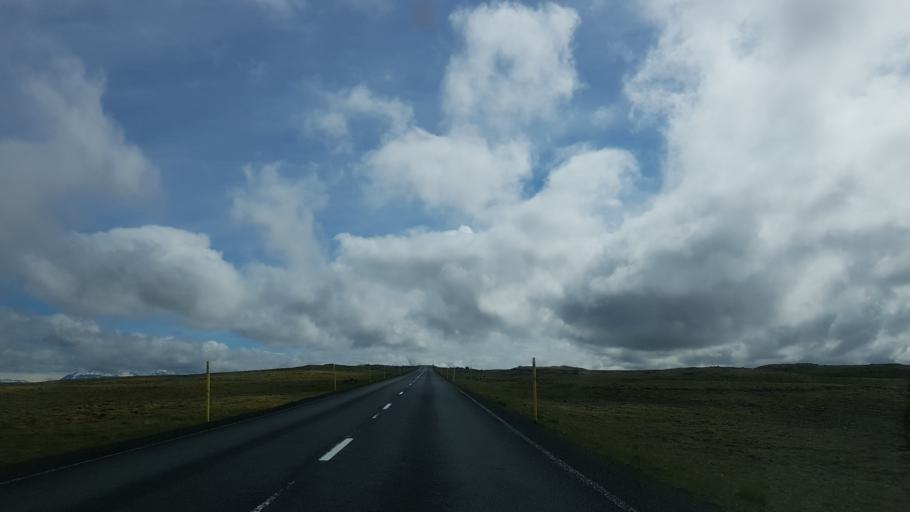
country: IS
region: West
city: Borgarnes
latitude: 64.9968
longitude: -21.0668
